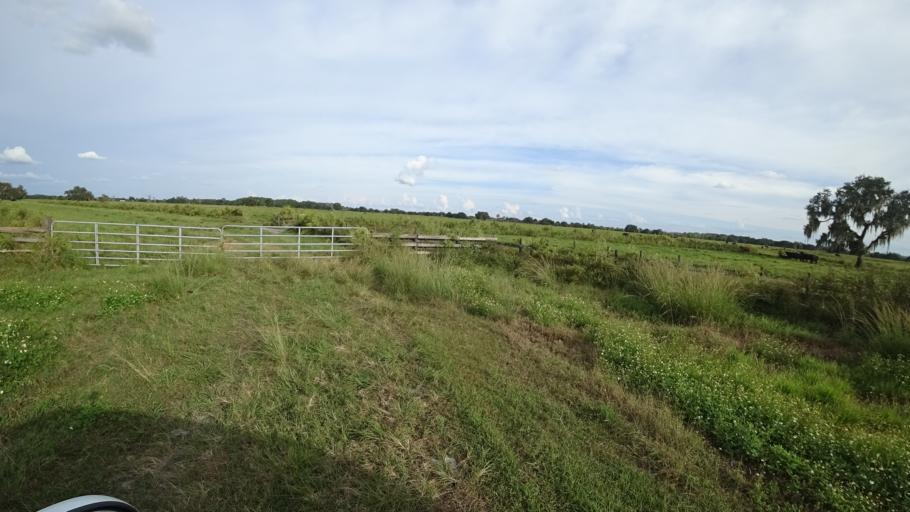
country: US
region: Florida
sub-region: Hillsborough County
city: Wimauma
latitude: 27.5517
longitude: -82.0923
